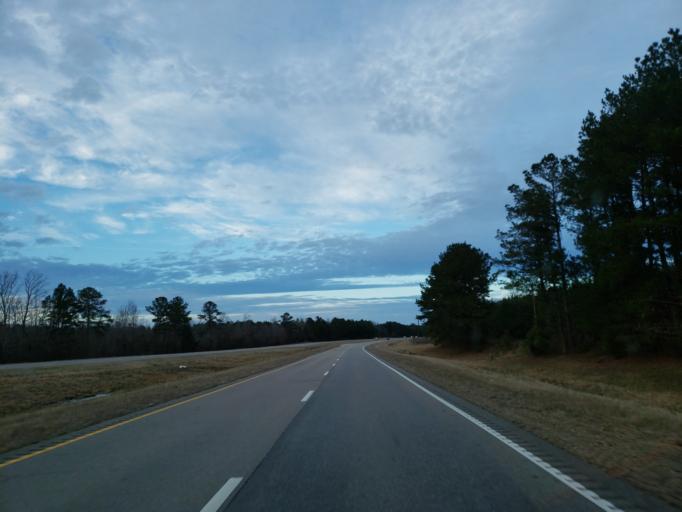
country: US
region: Mississippi
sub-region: Kemper County
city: De Kalb
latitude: 32.7177
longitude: -88.4790
